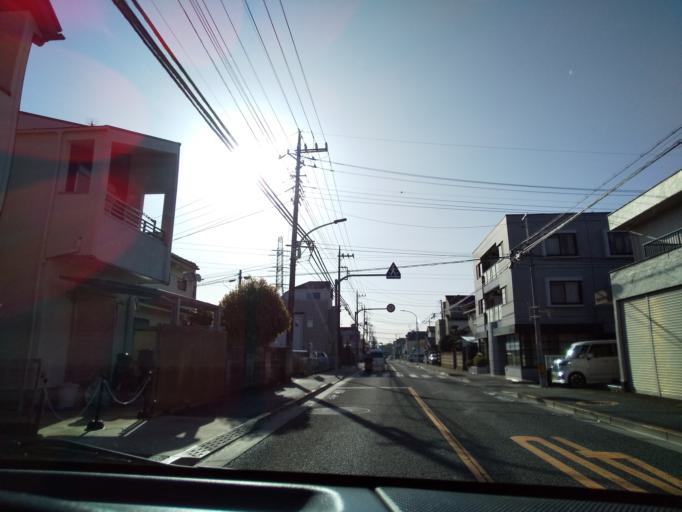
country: JP
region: Tokyo
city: Hino
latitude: 35.7006
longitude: 139.3841
